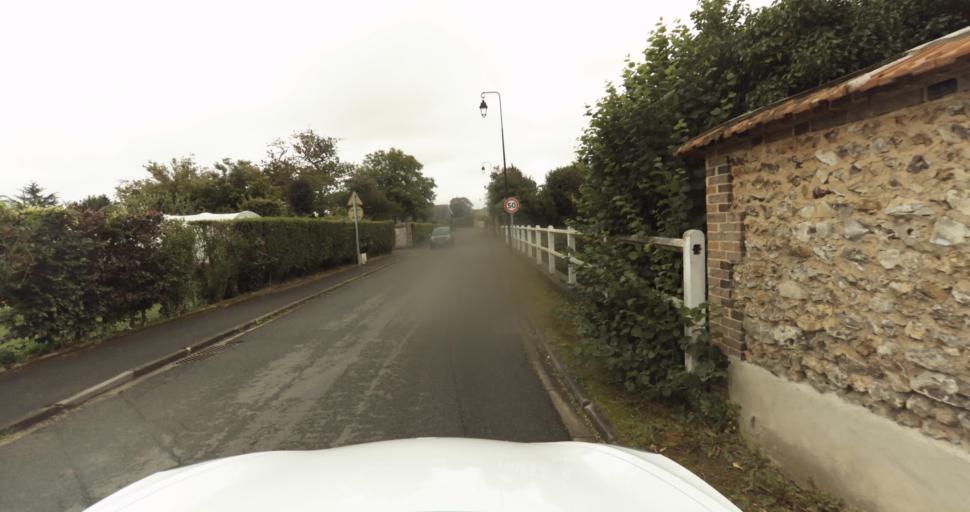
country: FR
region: Haute-Normandie
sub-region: Departement de l'Eure
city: Aviron
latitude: 49.0792
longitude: 1.0796
